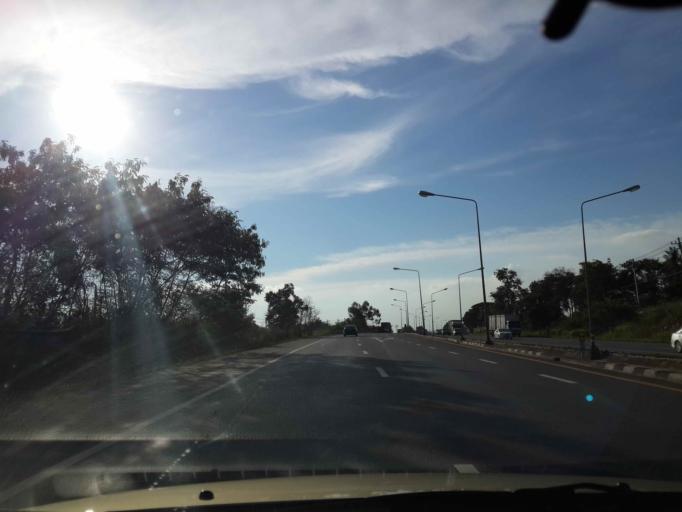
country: TH
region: Chon Buri
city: Phatthaya
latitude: 12.9273
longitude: 101.0039
